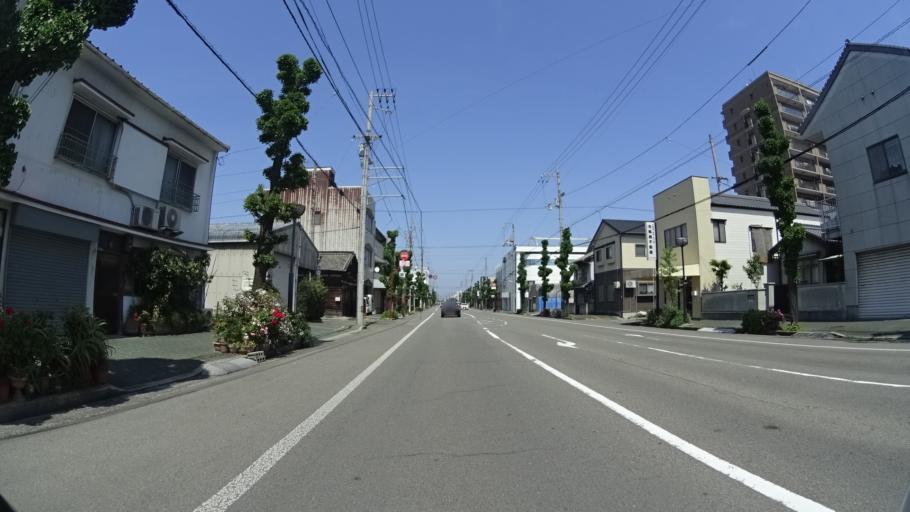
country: JP
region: Ehime
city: Saijo
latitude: 34.0602
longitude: 133.0037
